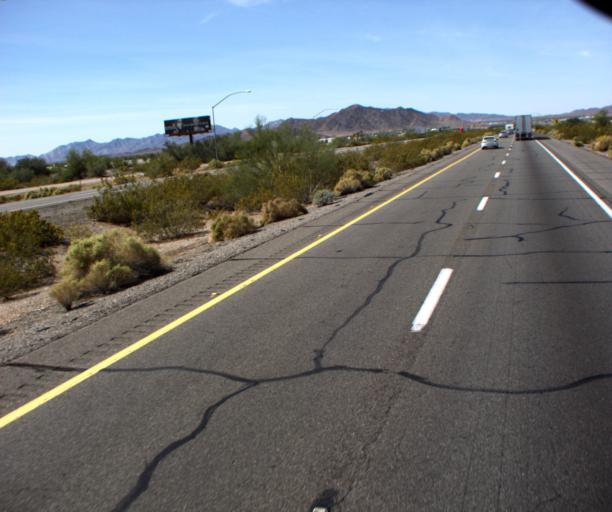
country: US
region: Arizona
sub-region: La Paz County
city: Quartzsite
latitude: 33.6654
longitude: -114.2026
